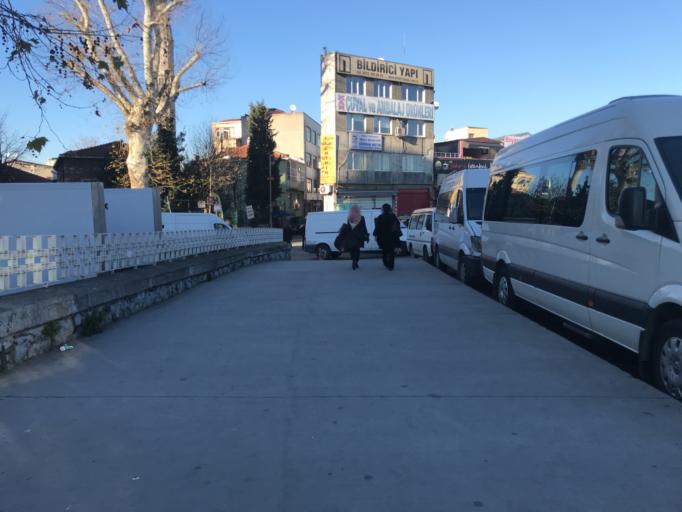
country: TR
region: Istanbul
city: Istanbul
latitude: 41.0222
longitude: 28.9603
